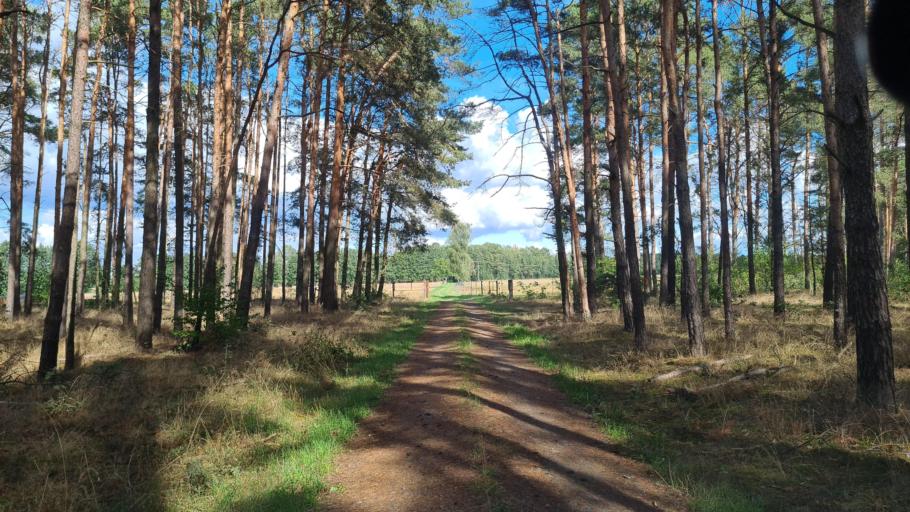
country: DE
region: Brandenburg
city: Finsterwalde
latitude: 51.6538
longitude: 13.7448
